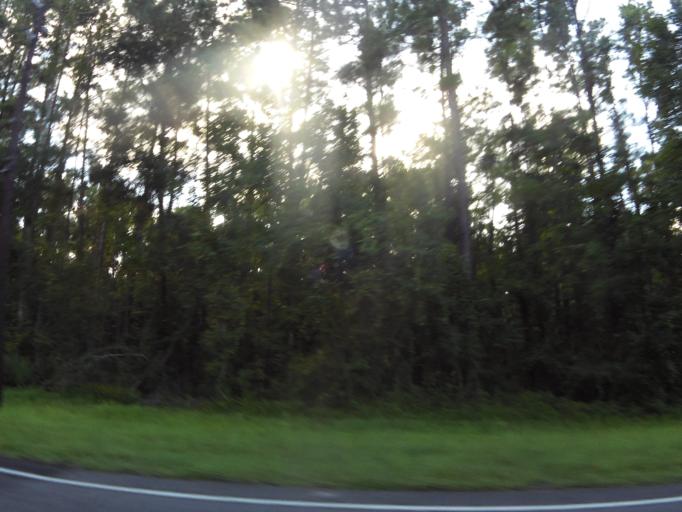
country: US
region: Georgia
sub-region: Camden County
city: Woodbine
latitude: 31.0435
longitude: -81.7298
